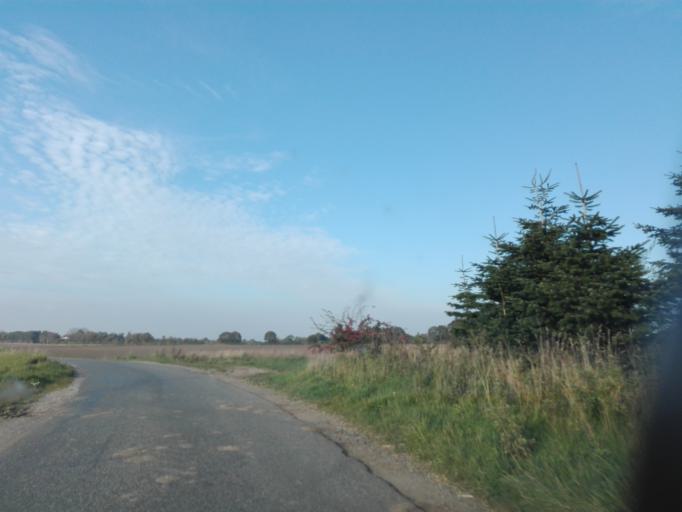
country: DK
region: Central Jutland
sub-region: Odder Kommune
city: Odder
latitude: 55.9862
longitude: 10.1988
